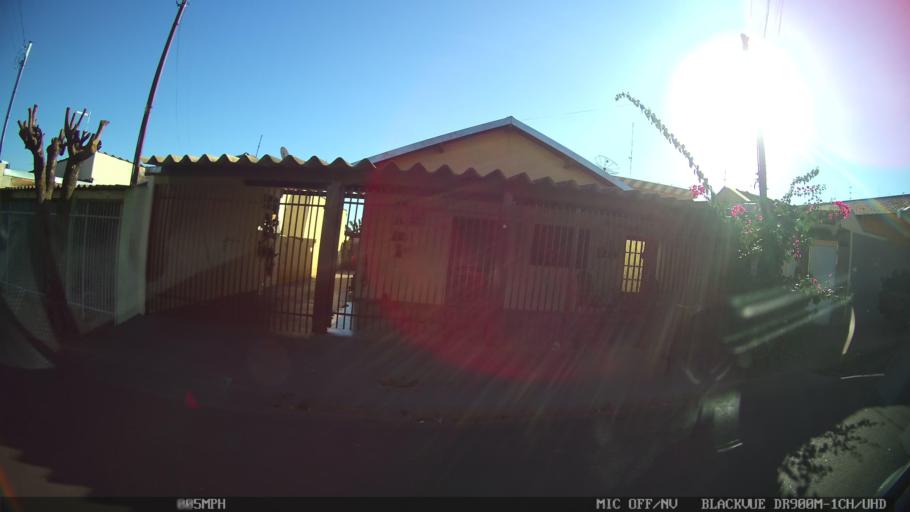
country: BR
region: Sao Paulo
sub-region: Olimpia
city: Olimpia
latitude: -20.7275
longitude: -48.9075
